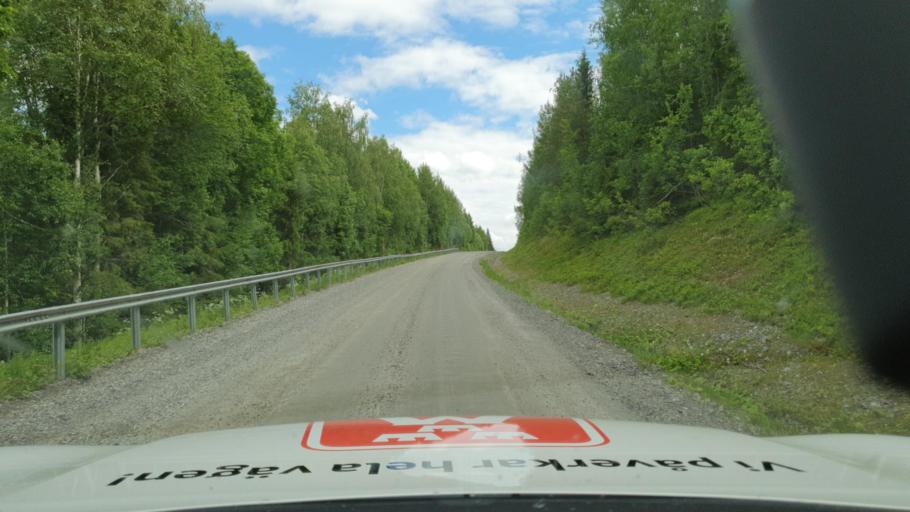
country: SE
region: Vaesterbotten
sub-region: Norsjo Kommun
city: Norsjoe
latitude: 64.8290
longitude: 19.5521
